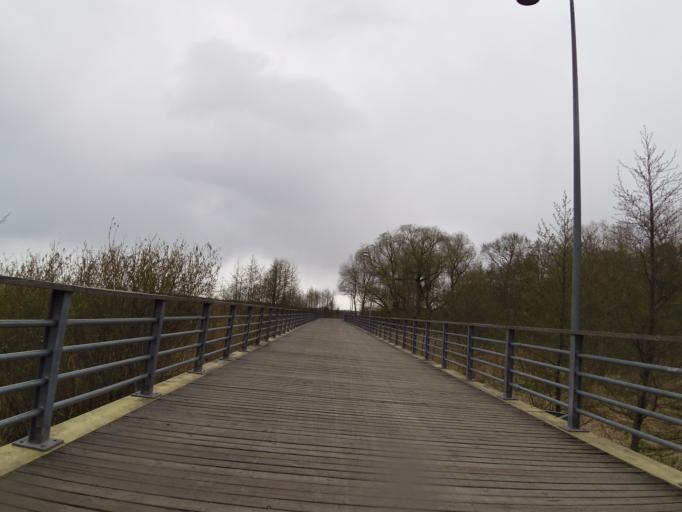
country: EE
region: Harju
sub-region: Tallinna linn
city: Tallinn
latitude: 59.4297
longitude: 24.6721
